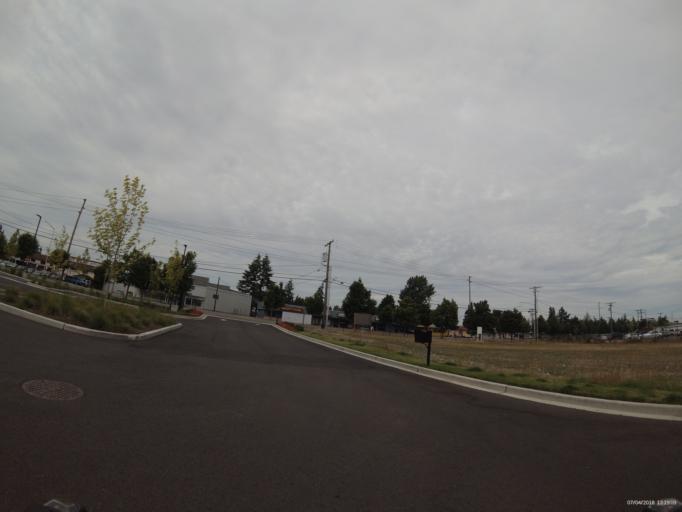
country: US
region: Washington
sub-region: Pierce County
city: McChord Air Force Base
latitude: 47.1505
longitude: -122.5011
